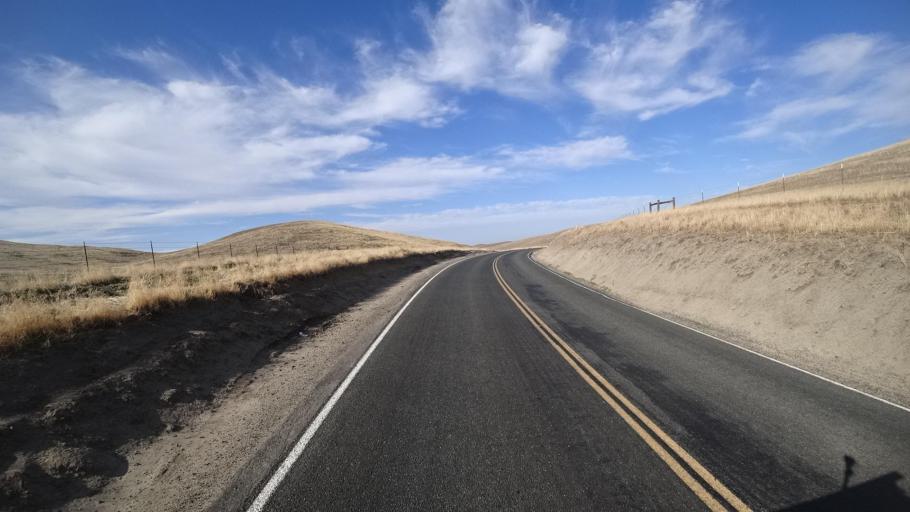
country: US
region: California
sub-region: Kern County
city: Oildale
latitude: 35.6109
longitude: -118.9293
